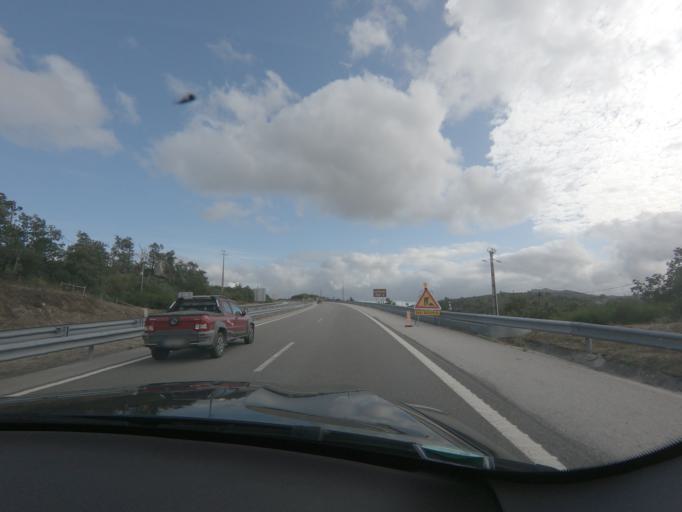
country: PT
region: Viseu
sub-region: Tarouca
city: Tarouca
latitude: 41.0130
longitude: -7.8843
